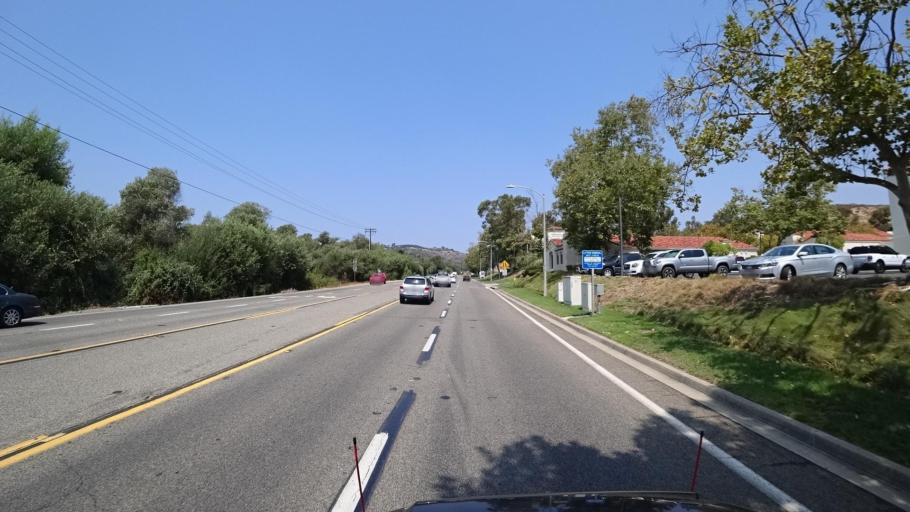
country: US
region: California
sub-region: San Diego County
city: Bonsall
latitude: 33.2955
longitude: -117.2232
